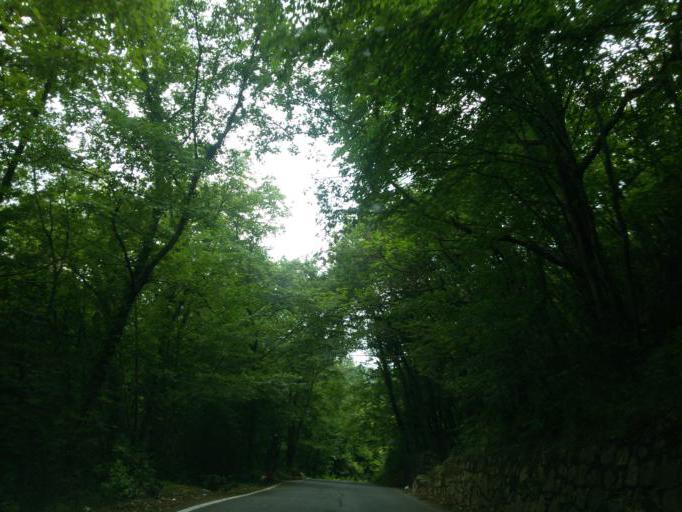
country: IT
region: Liguria
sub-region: Provincia di Genova
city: Piccarello
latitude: 44.4397
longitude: 9.0049
